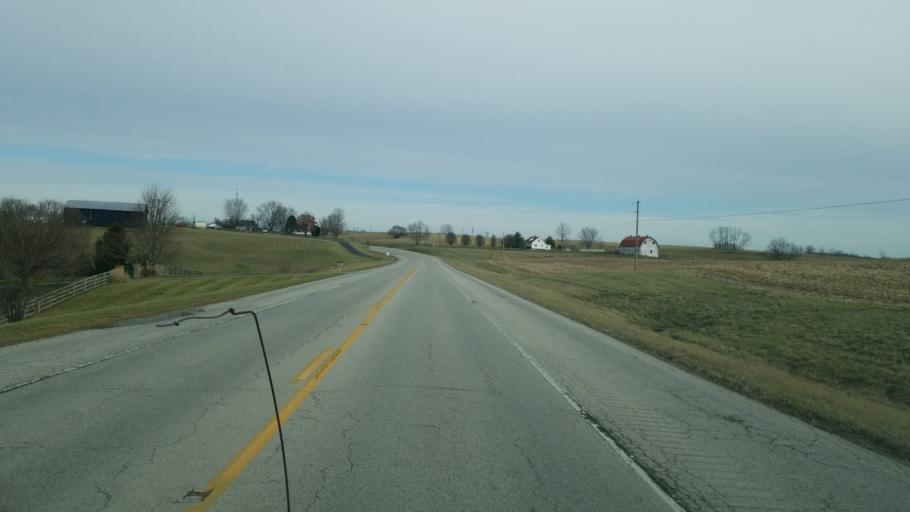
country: US
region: Kentucky
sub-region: Fleming County
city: Flemingsburg
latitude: 38.4863
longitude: -83.8620
